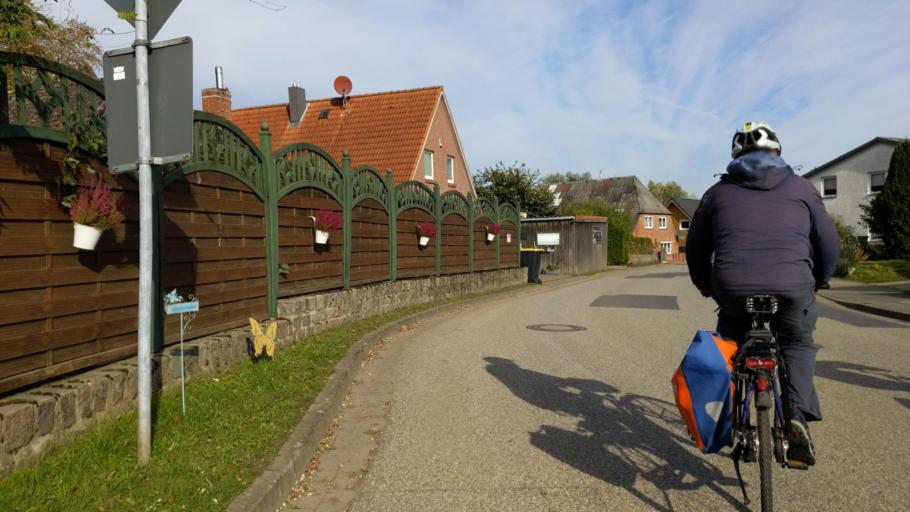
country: DE
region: Schleswig-Holstein
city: Zarpen
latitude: 53.8680
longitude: 10.5203
